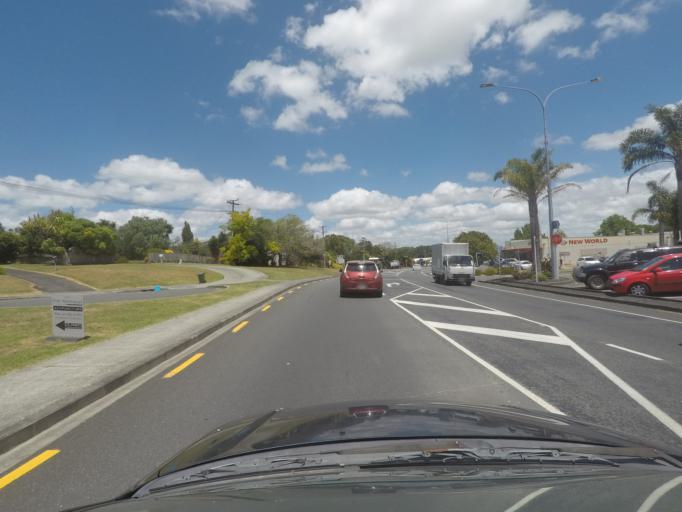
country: NZ
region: Northland
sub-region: Whangarei
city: Whangarei
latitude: -35.7552
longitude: 174.3686
